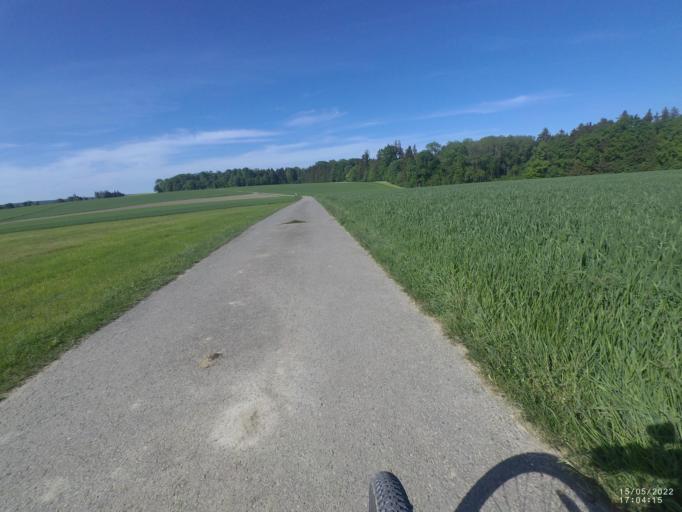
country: DE
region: Baden-Wuerttemberg
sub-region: Tuebingen Region
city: Setzingen
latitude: 48.5843
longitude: 10.1420
